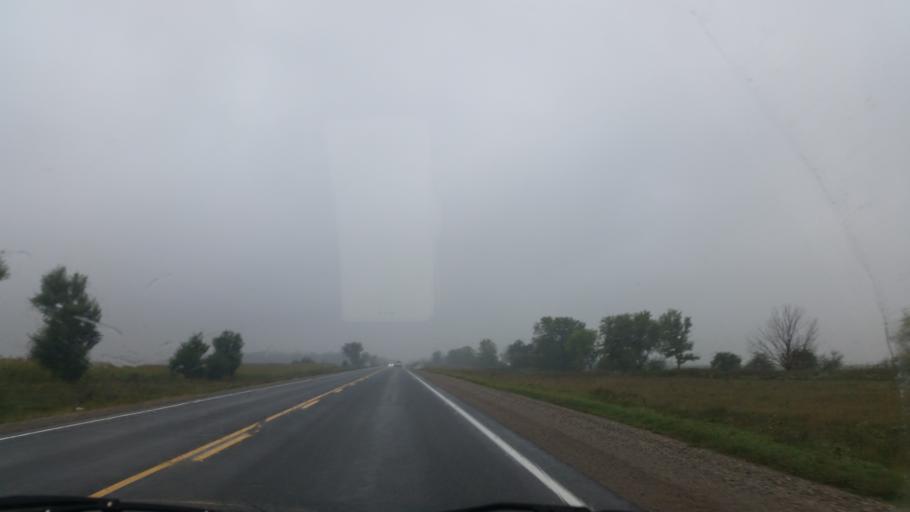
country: CA
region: Ontario
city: Stratford
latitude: 43.2564
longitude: -81.0785
